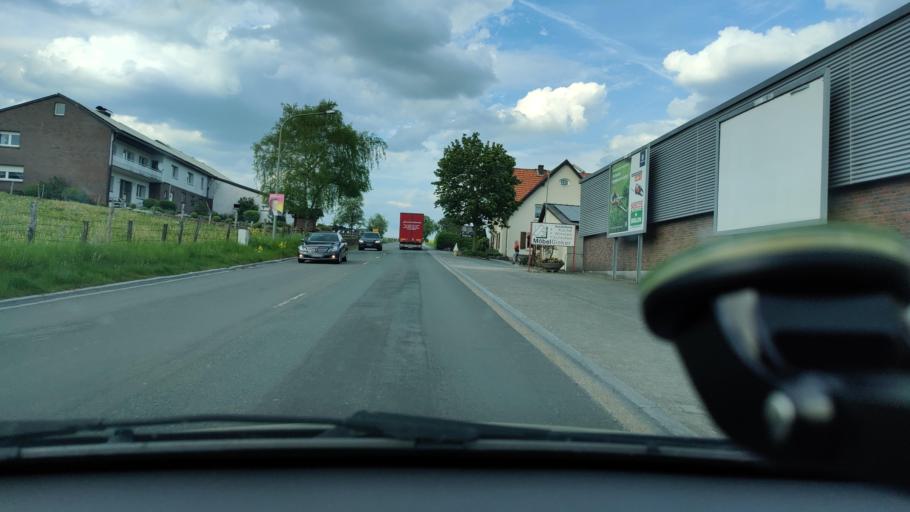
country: DE
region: North Rhine-Westphalia
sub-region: Regierungsbezirk Detmold
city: Wunnenberg
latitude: 51.4619
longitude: 8.6325
